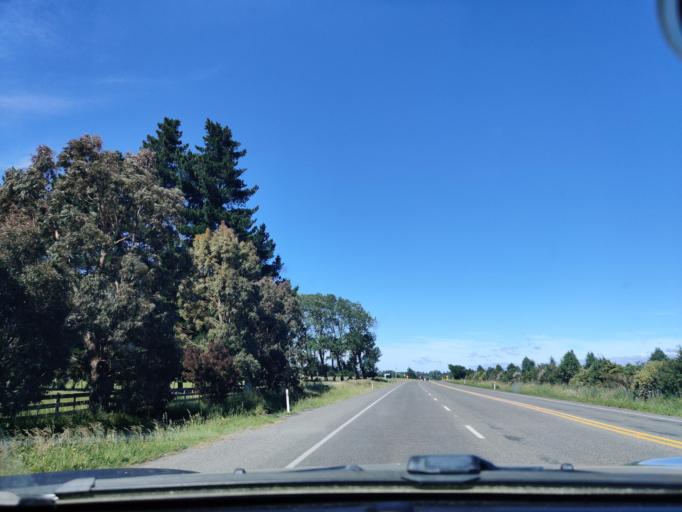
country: NZ
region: Wellington
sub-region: Masterton District
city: Masterton
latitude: -41.0452
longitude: 175.5062
